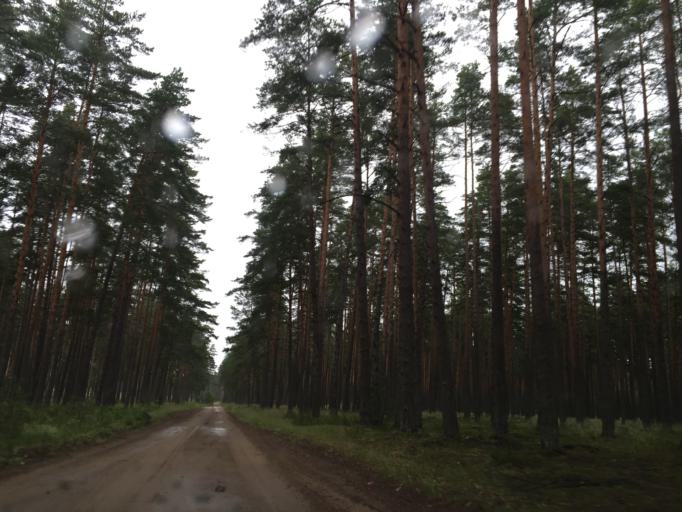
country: LV
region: Riga
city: Jaunciems
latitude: 57.0557
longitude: 24.2028
